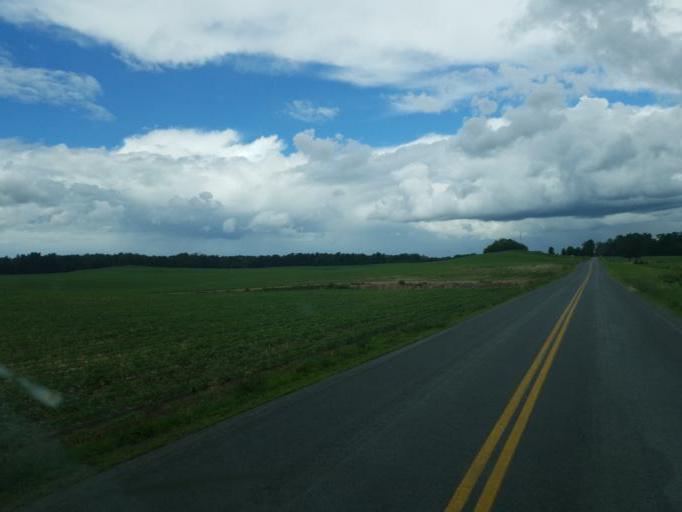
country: US
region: New York
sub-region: Wayne County
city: Lyons
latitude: 42.9819
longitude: -76.9354
